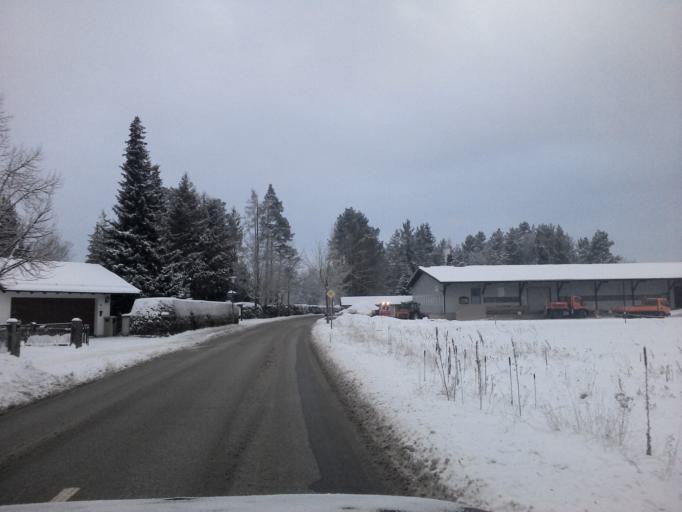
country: DE
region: Bavaria
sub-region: Upper Bavaria
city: Seeshaupt
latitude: 47.8210
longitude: 11.2893
